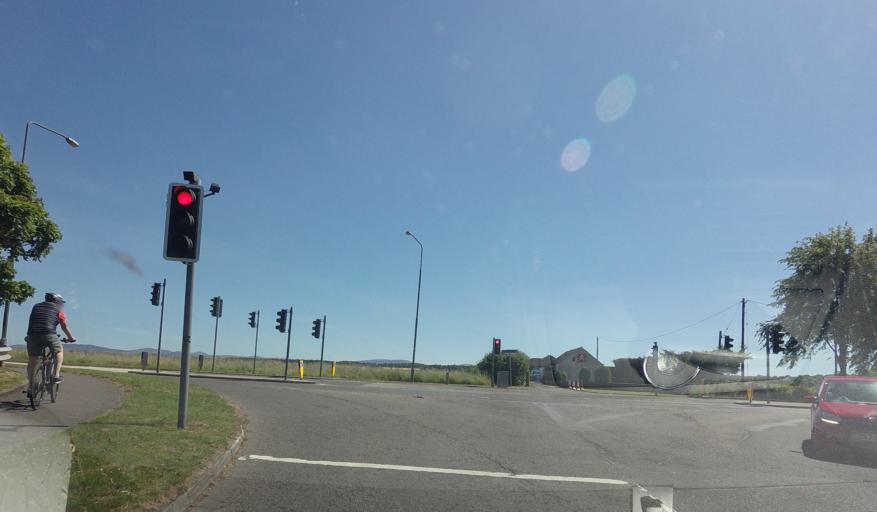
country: GB
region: Scotland
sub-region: West Lothian
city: Broxburn
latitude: 55.9289
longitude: -3.4837
